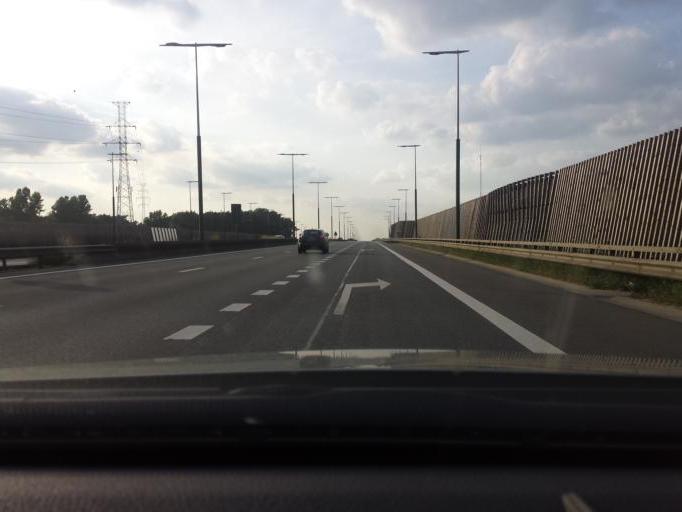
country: BE
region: Flanders
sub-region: Provincie Limburg
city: Lummen
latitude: 50.9917
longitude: 5.2294
